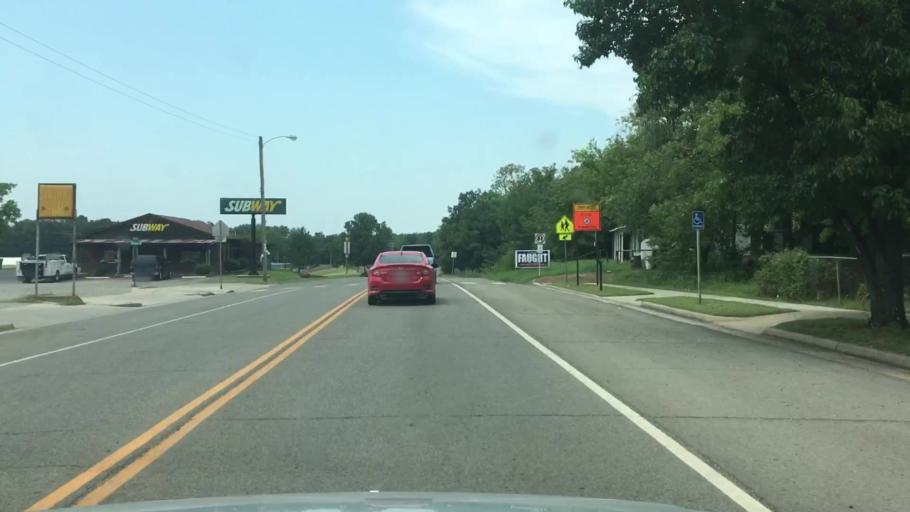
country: US
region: Oklahoma
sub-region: Muskogee County
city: Fort Gibson
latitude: 35.9328
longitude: -95.1445
